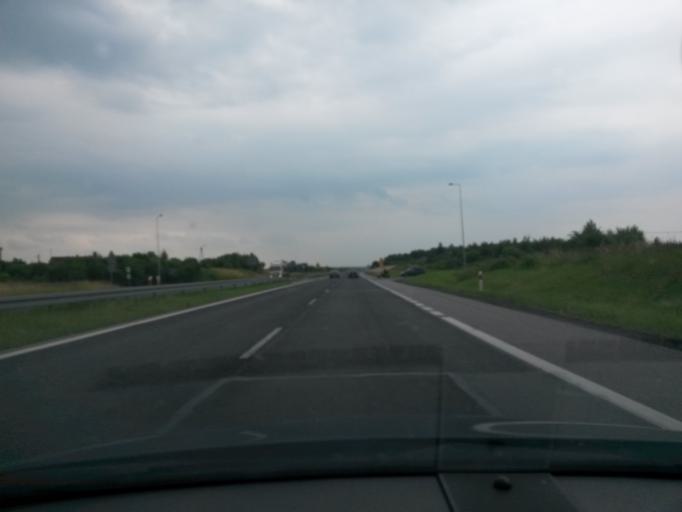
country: PL
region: Silesian Voivodeship
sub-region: Powiat czestochowski
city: Mykanow
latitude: 50.9246
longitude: 19.2245
